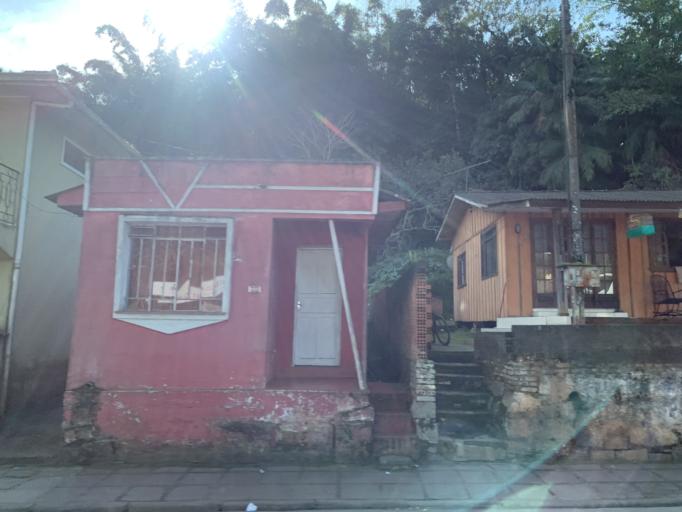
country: BR
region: Parana
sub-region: Antonina
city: Antonina
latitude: -25.4319
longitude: -48.7206
